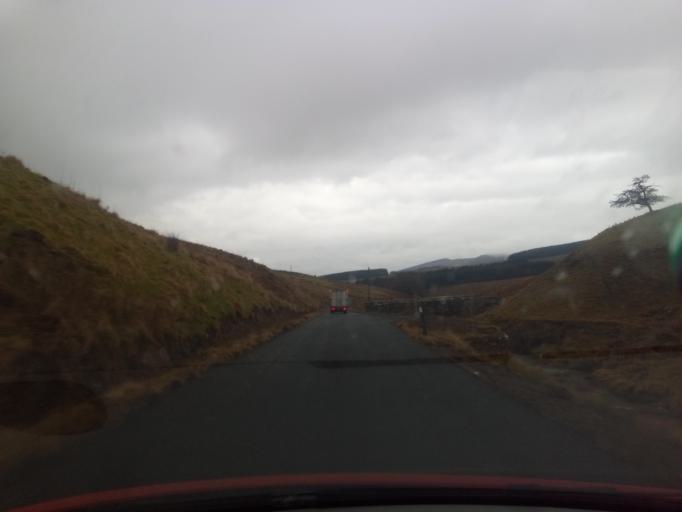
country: GB
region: Scotland
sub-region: The Scottish Borders
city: Hawick
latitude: 55.2751
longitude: -2.6817
